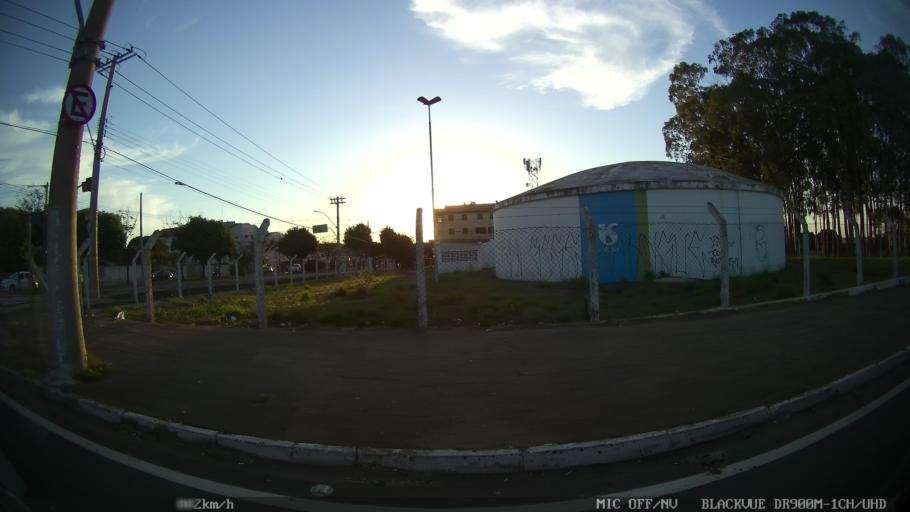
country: BR
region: Sao Paulo
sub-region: Franca
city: Franca
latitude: -20.5024
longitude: -47.4088
